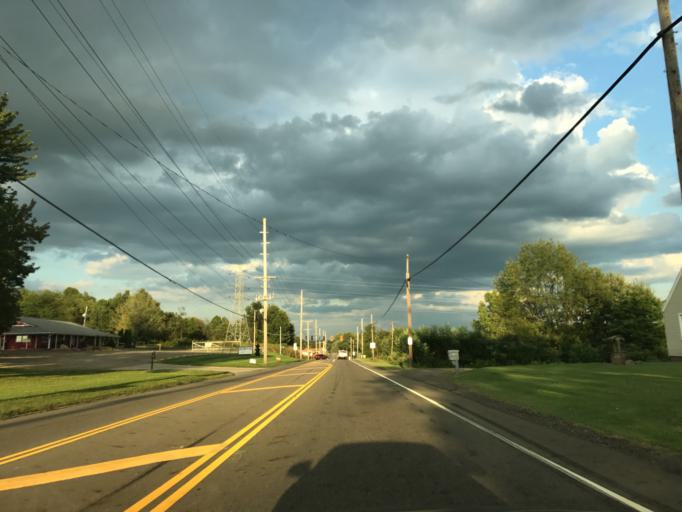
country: US
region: Ohio
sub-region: Stark County
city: East Canton
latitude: 40.7877
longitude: -81.3033
